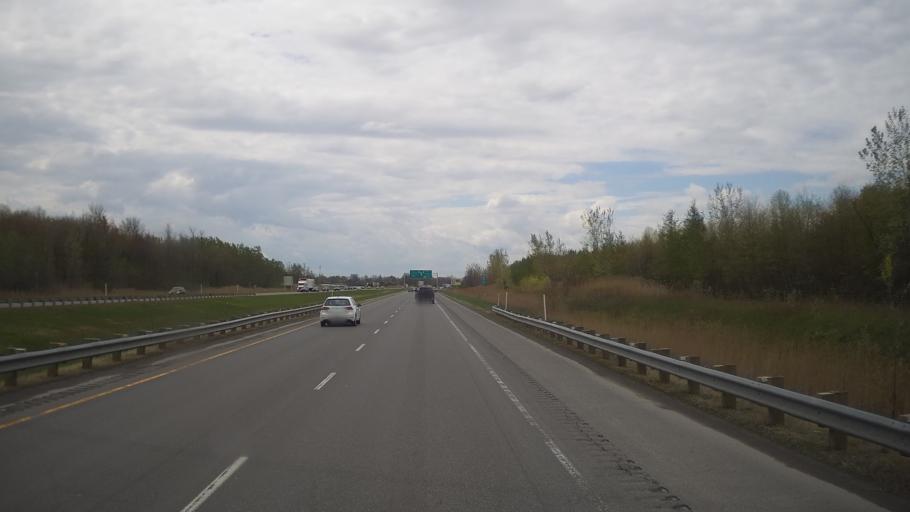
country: CA
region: Quebec
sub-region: Monteregie
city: La Prairie
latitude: 45.3939
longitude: -73.4675
